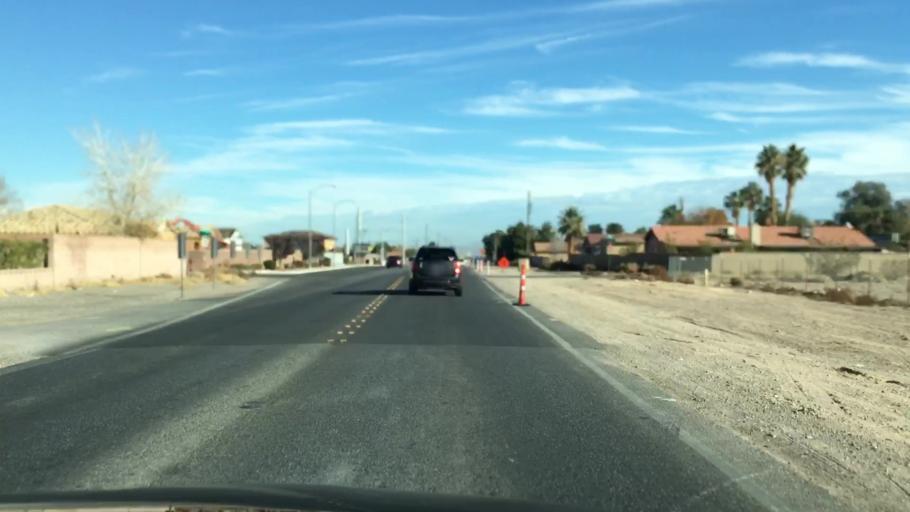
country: US
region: Nevada
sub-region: Clark County
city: Enterprise
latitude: 36.0572
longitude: -115.1933
